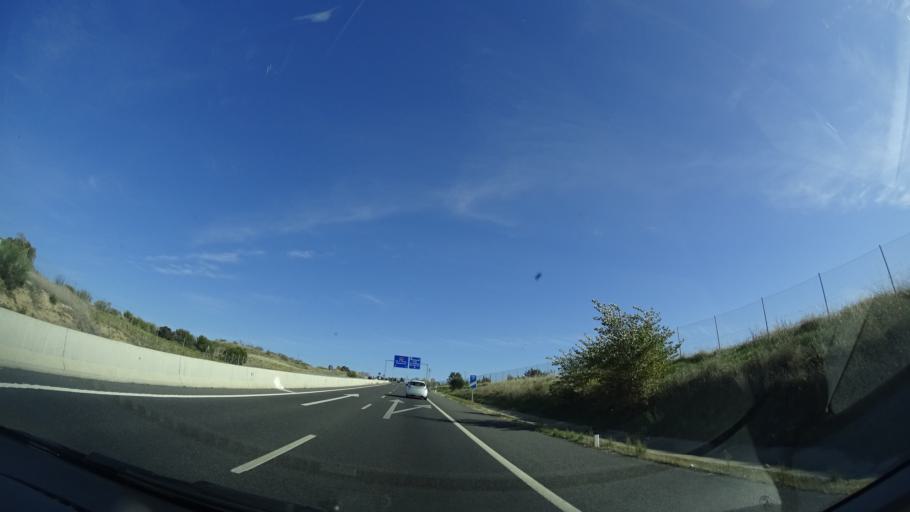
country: ES
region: Madrid
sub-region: Provincia de Madrid
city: Majadahonda
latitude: 40.4796
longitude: -3.9042
